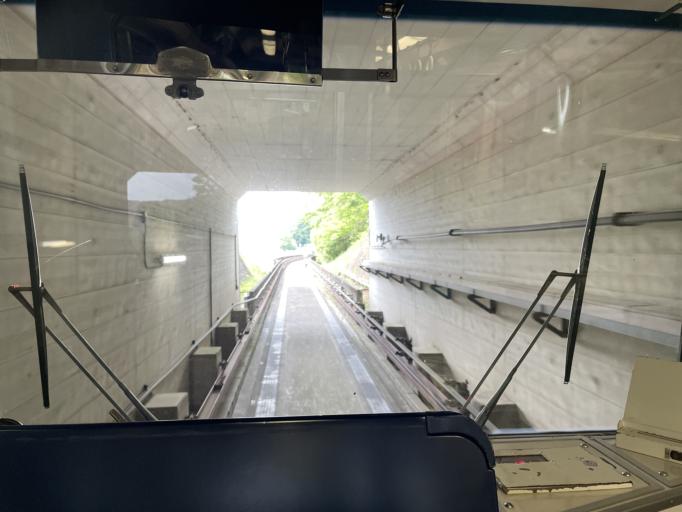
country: JP
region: Tokyo
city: Higashimurayama-shi
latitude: 35.7691
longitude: 139.4221
